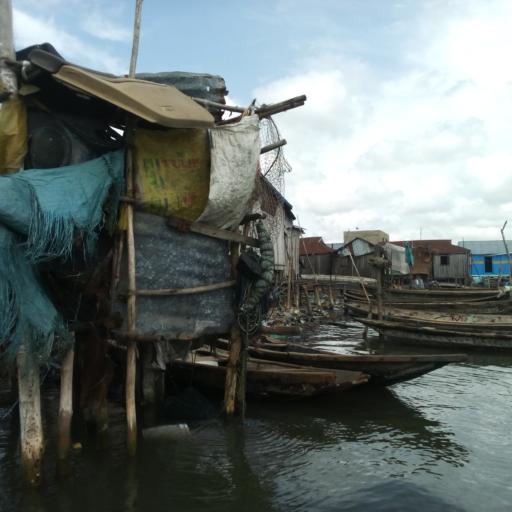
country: BJ
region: Littoral
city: Cotonou
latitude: 6.3923
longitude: 2.4339
